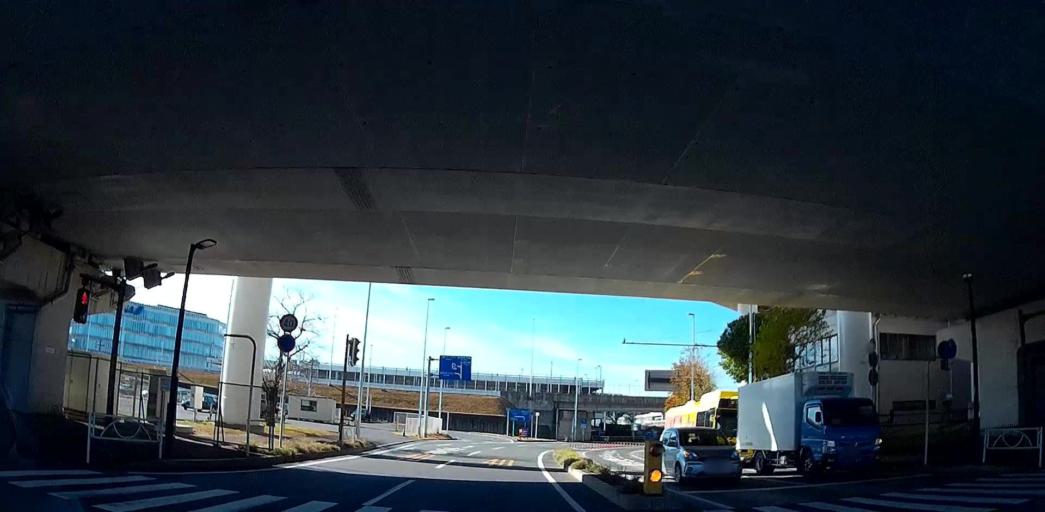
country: JP
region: Chiba
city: Narita
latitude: 35.7675
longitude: 140.3897
